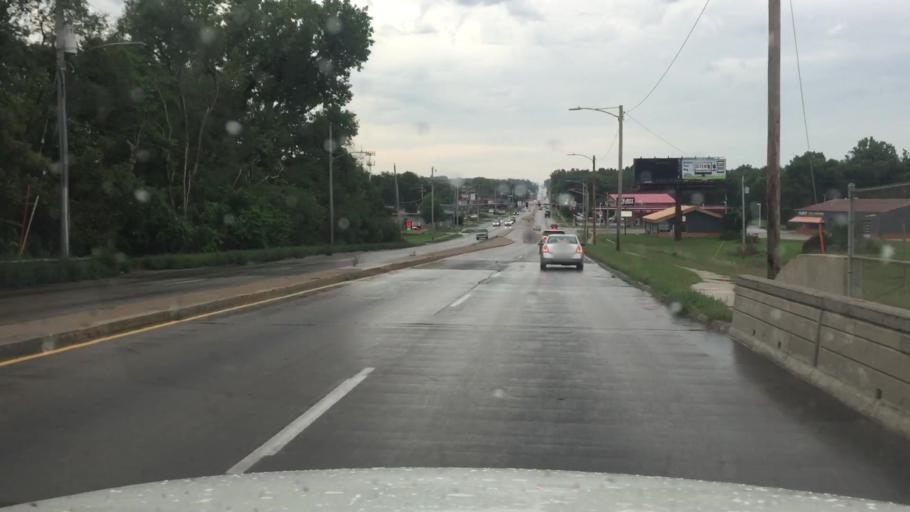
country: US
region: Iowa
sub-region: Polk County
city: Des Moines
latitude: 41.5834
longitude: -93.5970
